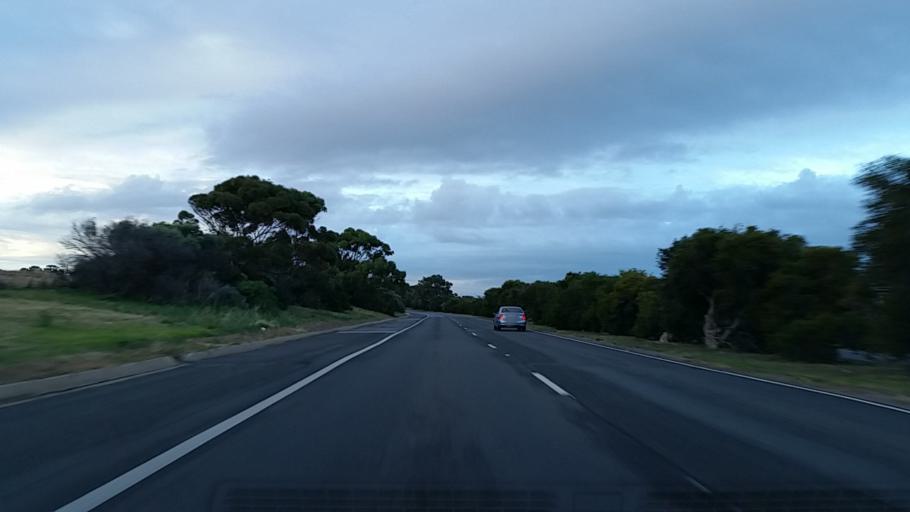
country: AU
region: South Australia
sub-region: Marion
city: Trott Park
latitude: -35.0658
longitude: 138.5320
